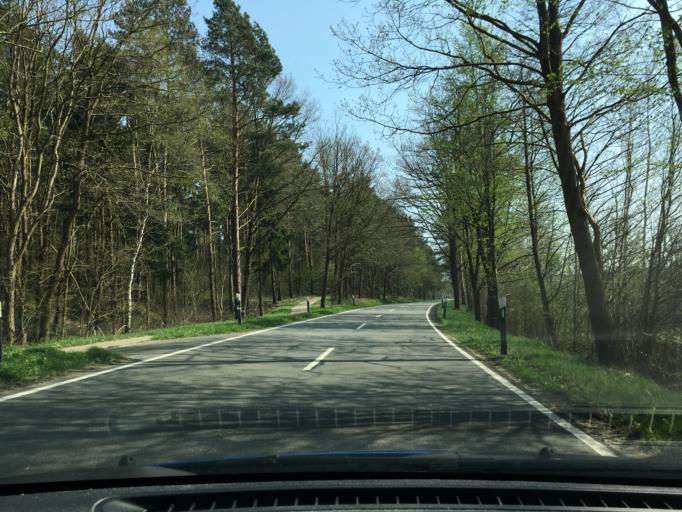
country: DE
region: Lower Saxony
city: Sudergellersen
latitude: 53.1968
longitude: 10.3069
